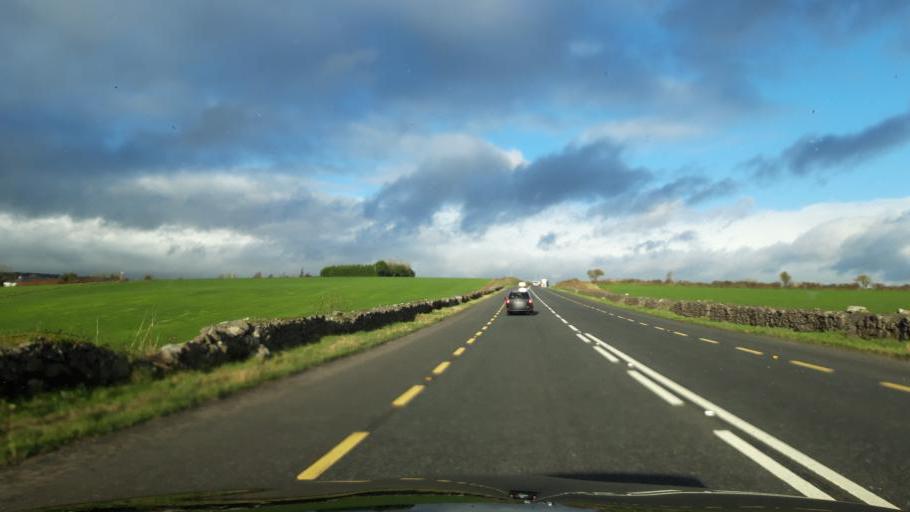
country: IE
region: Leinster
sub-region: An Mhi
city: Slane
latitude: 53.7318
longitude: -6.5140
